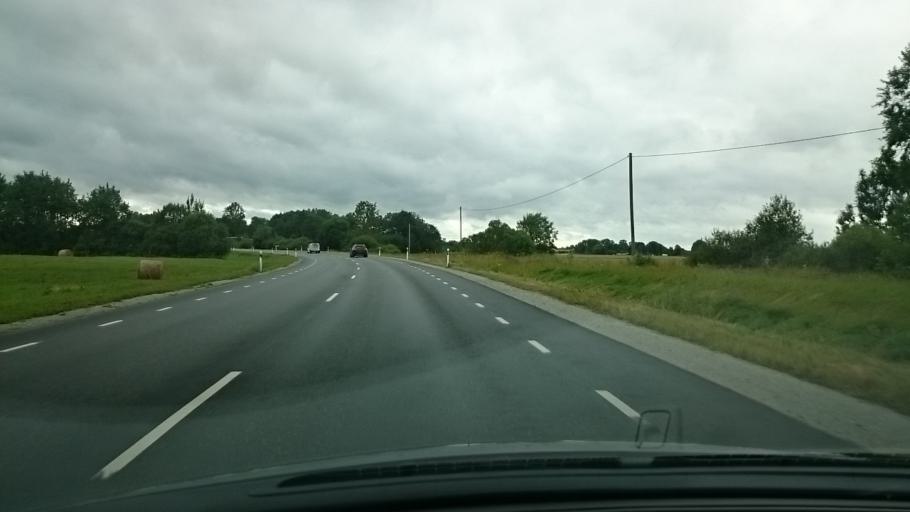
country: EE
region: Harju
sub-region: Keila linn
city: Keila
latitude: 59.2987
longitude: 24.3476
